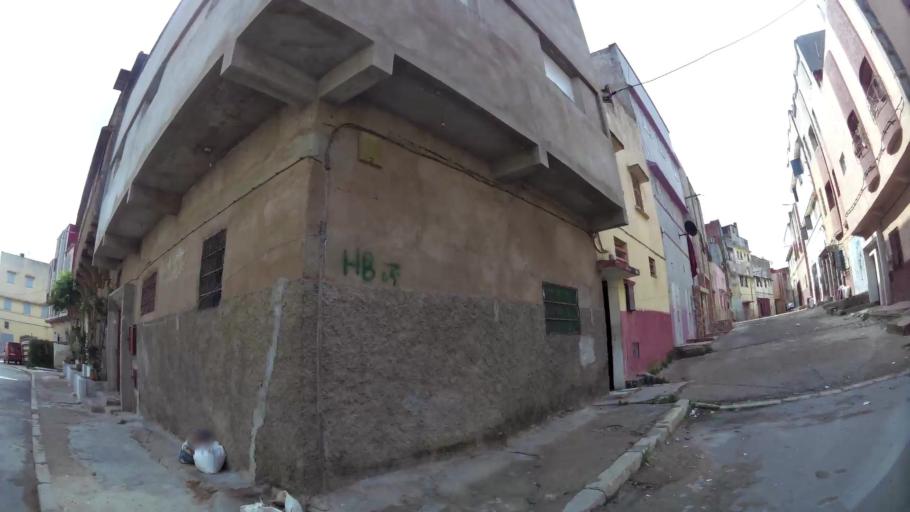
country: MA
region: Rabat-Sale-Zemmour-Zaer
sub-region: Khemisset
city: Tiflet
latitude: 33.8950
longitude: -6.3136
